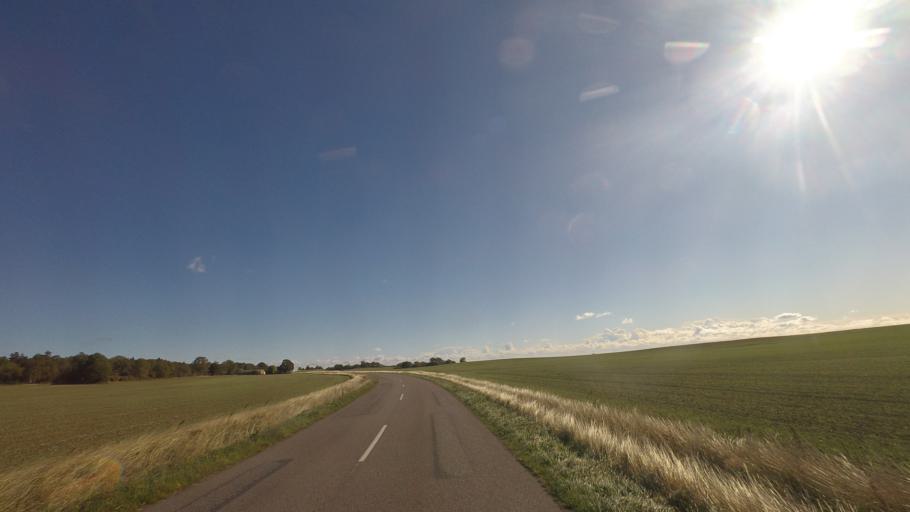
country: DK
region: Capital Region
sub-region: Bornholm Kommune
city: Nexo
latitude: 55.0774
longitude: 15.0870
